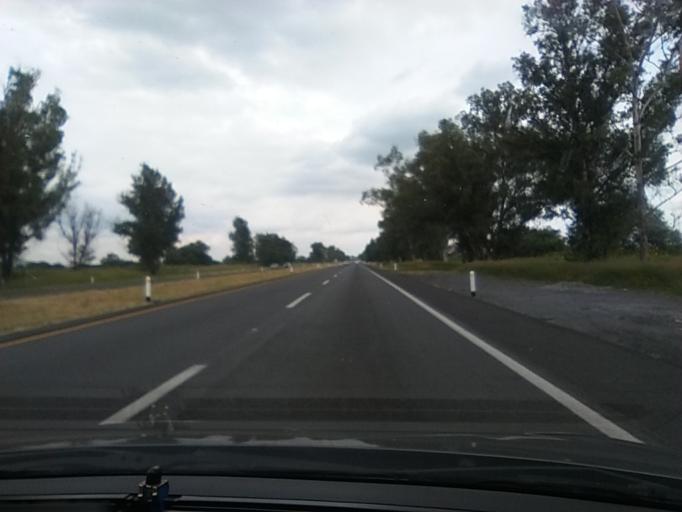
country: MX
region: Jalisco
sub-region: Ocotlan
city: Joconoxtle (La Tuna)
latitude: 20.3770
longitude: -102.6784
